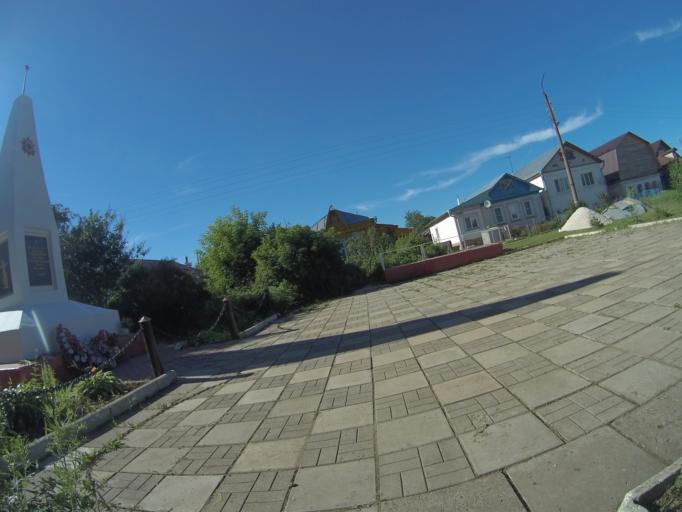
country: RU
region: Vladimir
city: Bogolyubovo
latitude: 56.2110
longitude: 40.5133
